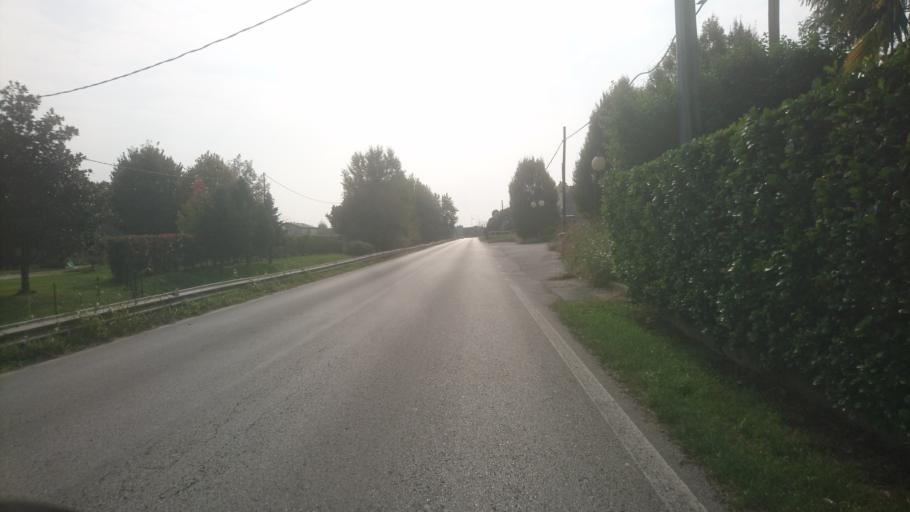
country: IT
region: Veneto
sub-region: Provincia di Vicenza
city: Quinto Vicentino
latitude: 45.5775
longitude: 11.6456
